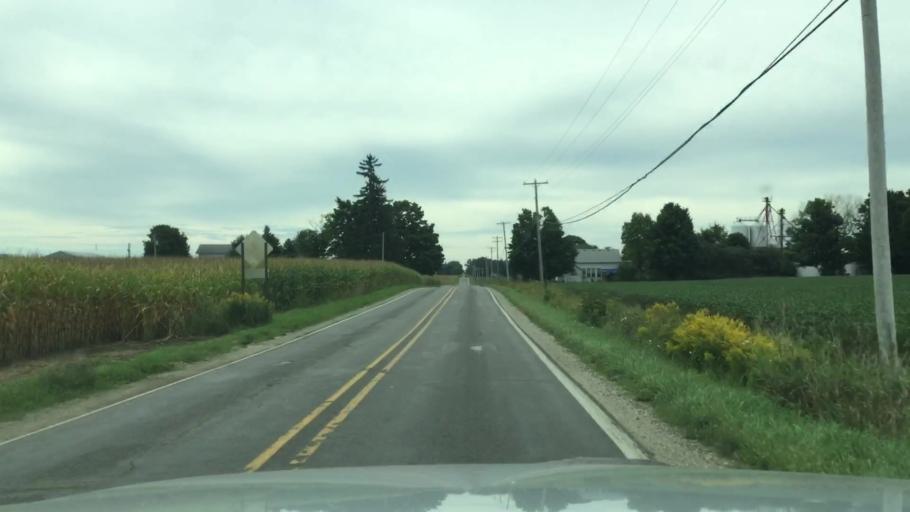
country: US
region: Michigan
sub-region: Shiawassee County
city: Durand
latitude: 42.9493
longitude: -83.9890
